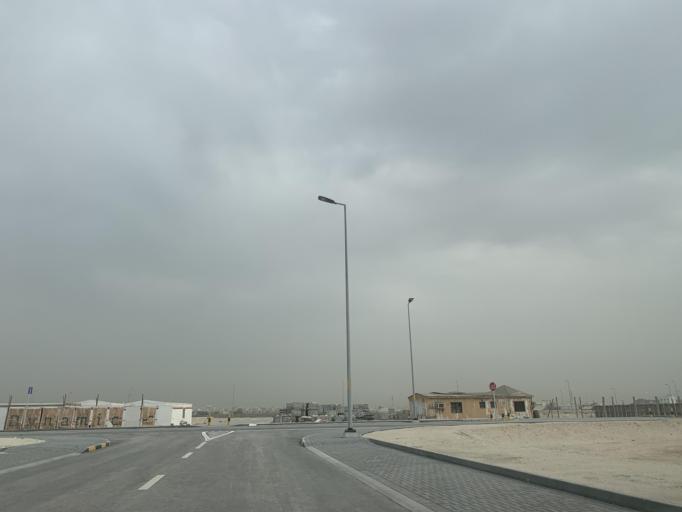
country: BH
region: Northern
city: Madinat `Isa
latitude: 26.1868
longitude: 50.5090
